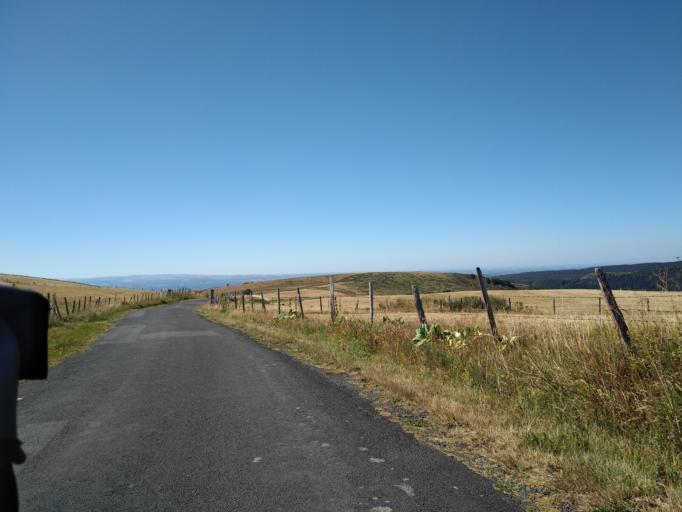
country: FR
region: Auvergne
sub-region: Departement du Cantal
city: Pierrefort
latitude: 45.0178
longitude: 2.8178
